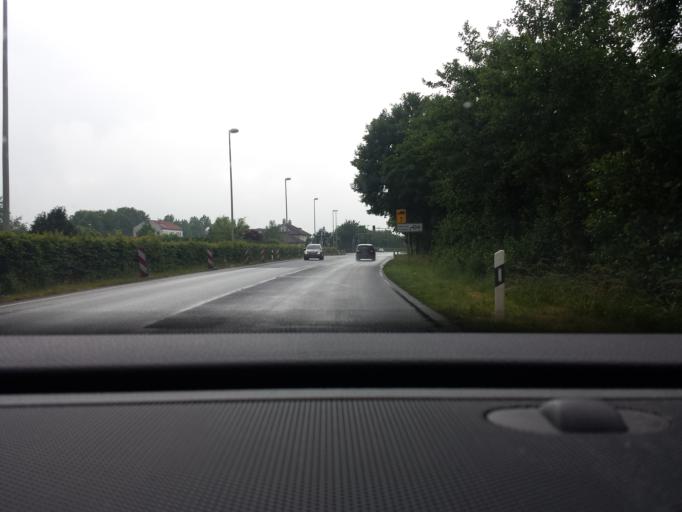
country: DE
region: North Rhine-Westphalia
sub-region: Regierungsbezirk Munster
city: Ahaus
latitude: 52.0693
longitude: 7.0038
